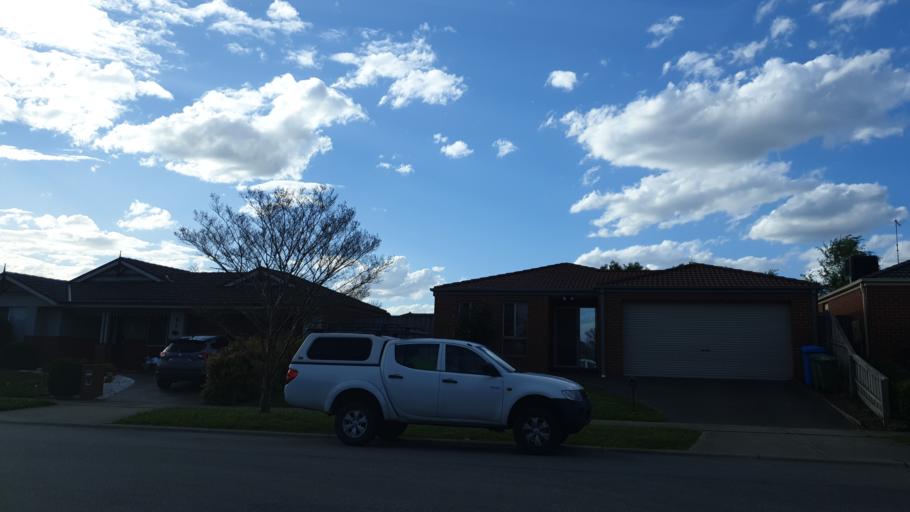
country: AU
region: Victoria
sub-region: Casey
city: Cranbourne North
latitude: -38.0877
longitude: 145.2874
